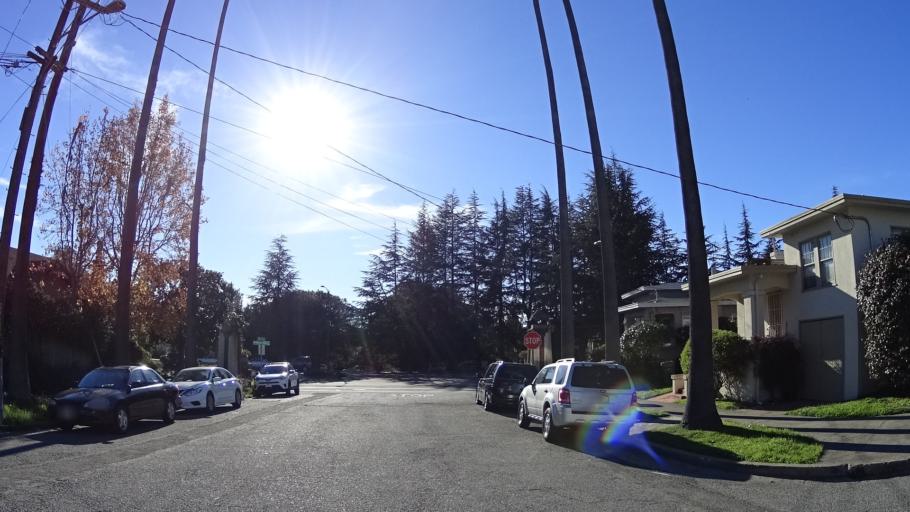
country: US
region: California
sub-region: Alameda County
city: Piedmont
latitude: 37.8298
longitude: -122.2463
